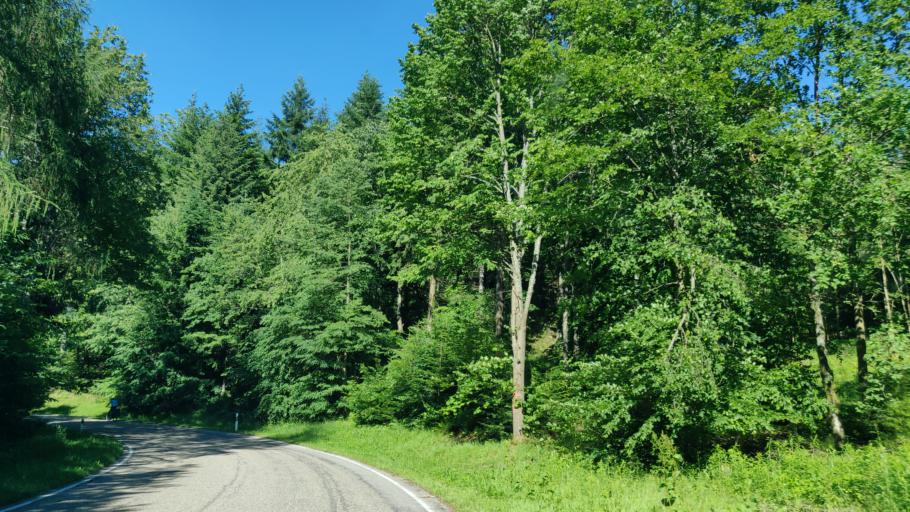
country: DE
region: Baden-Wuerttemberg
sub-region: Karlsruhe Region
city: Gernsbach
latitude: 48.7484
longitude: 8.3123
